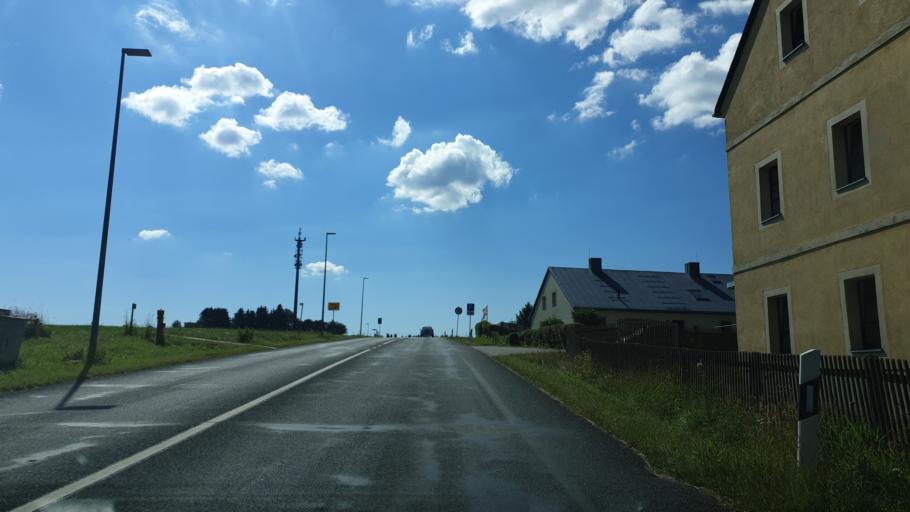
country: DE
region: Saxony
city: Marienberg
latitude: 50.6631
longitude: 13.1444
